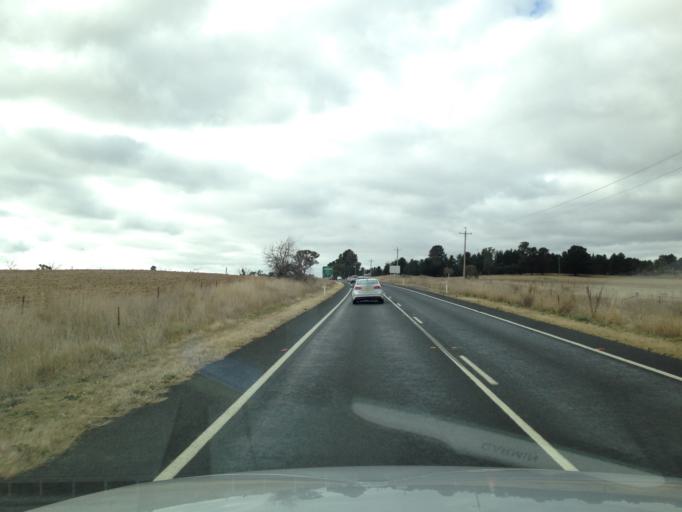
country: AU
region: New South Wales
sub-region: Cooma-Monaro
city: Cooma
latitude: -36.2489
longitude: 149.0464
